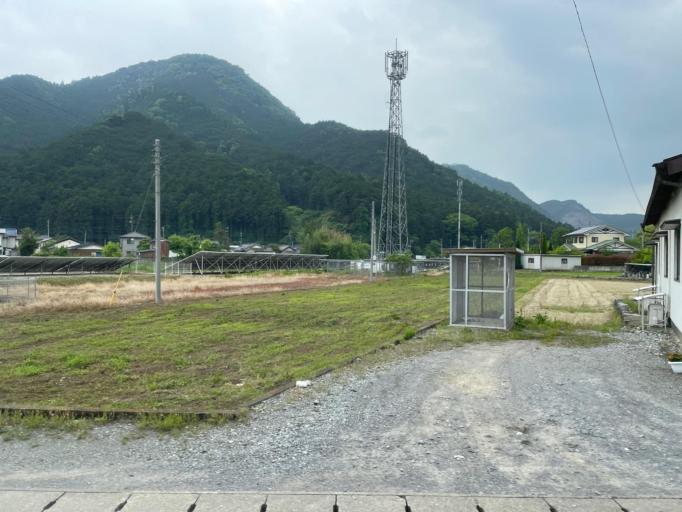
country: JP
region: Tochigi
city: Tanuma
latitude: 36.4521
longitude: 139.6395
